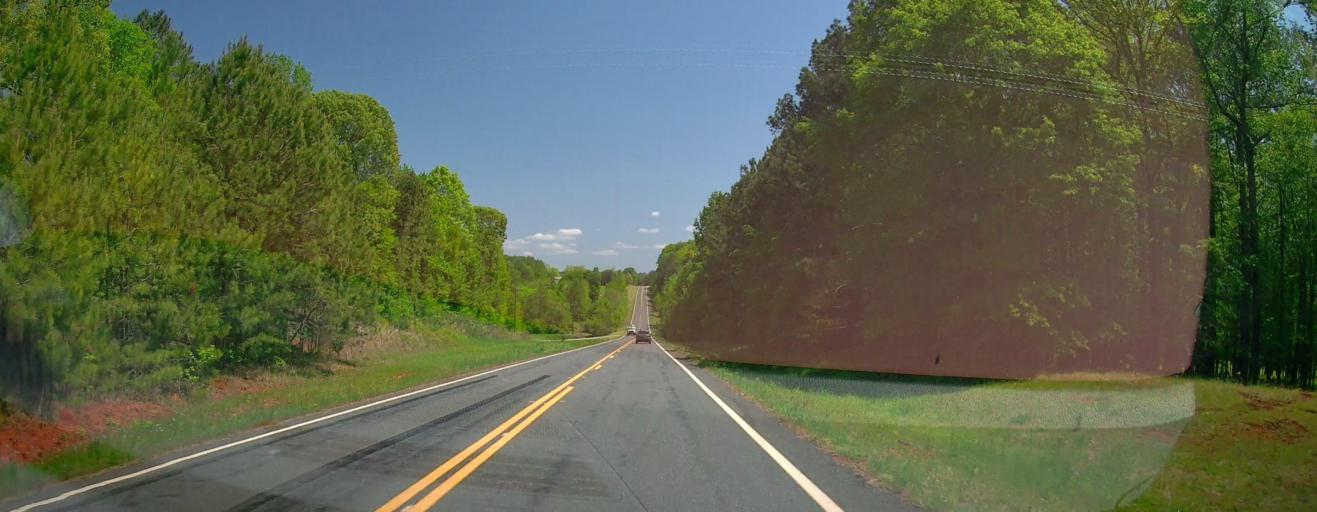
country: US
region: Georgia
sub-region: Jasper County
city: Monticello
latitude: 33.2714
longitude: -83.5901
